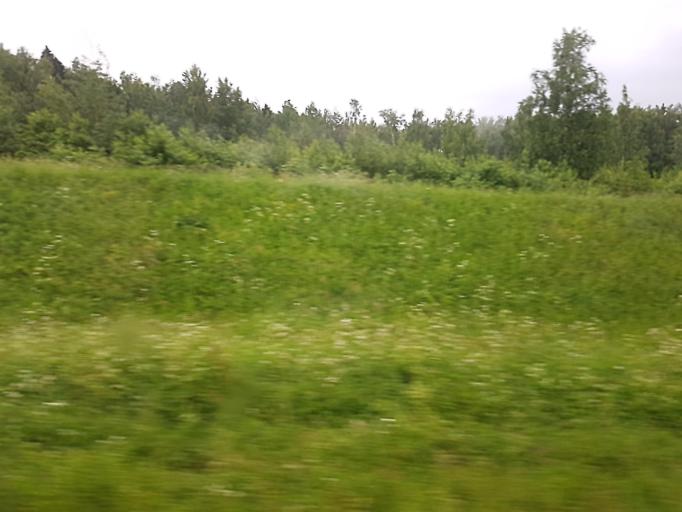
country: RU
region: Moskovskaya
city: Lesnoy Gorodok
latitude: 55.6431
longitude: 37.2396
